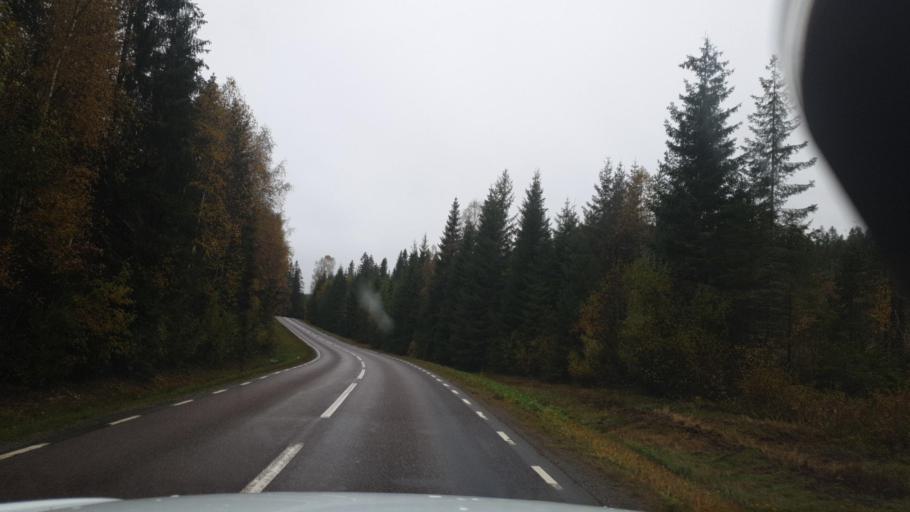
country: SE
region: Vaermland
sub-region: Eda Kommun
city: Amotfors
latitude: 59.6682
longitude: 12.3832
